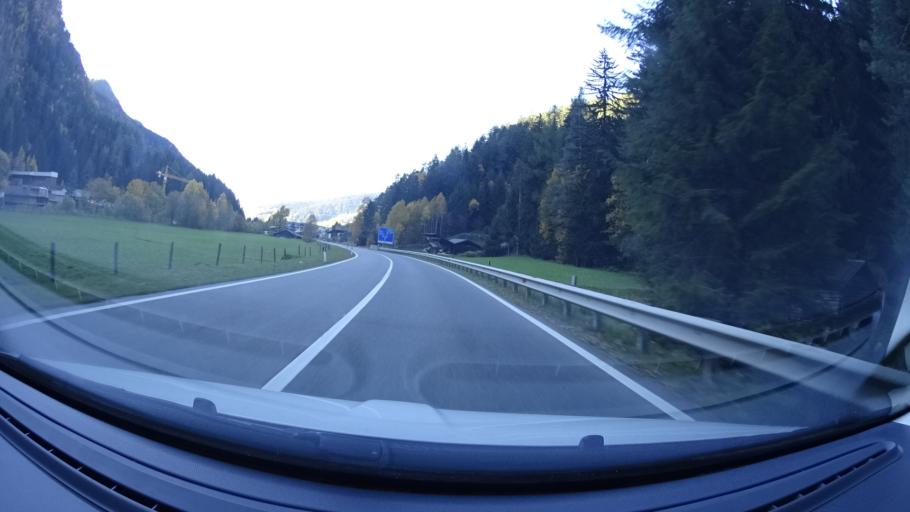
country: IT
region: Trentino-Alto Adige
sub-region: Bolzano
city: Ortisei
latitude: 46.5827
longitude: 11.6377
